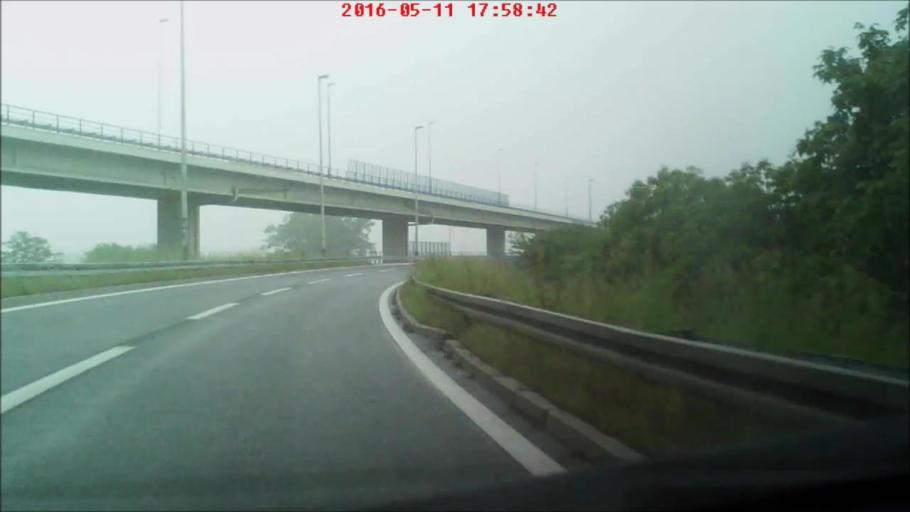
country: HR
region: Grad Zagreb
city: Lucko
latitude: 45.7614
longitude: 15.8969
